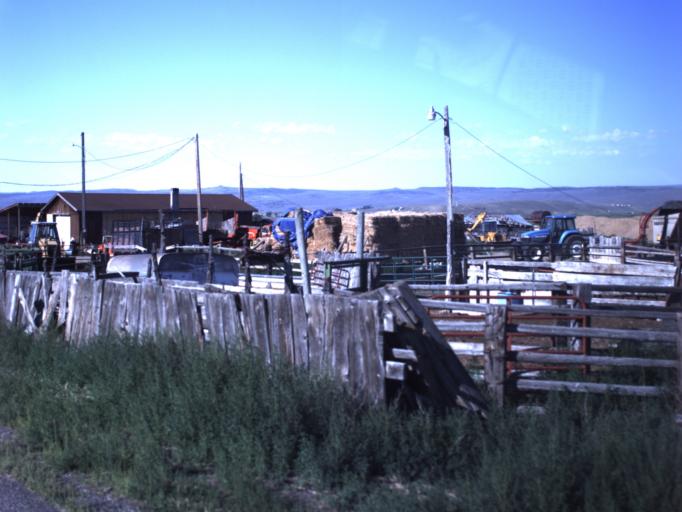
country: US
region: Utah
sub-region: Wayne County
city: Loa
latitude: 38.4470
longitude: -111.6158
